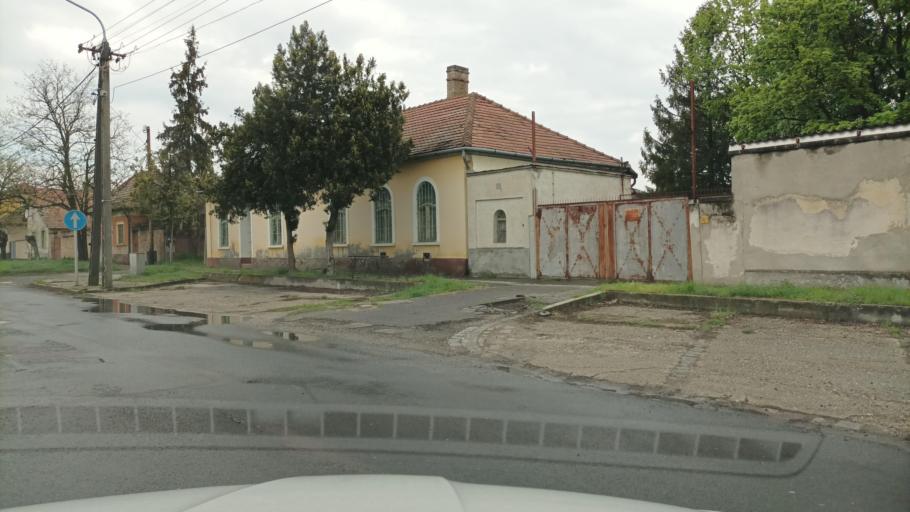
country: HU
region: Pest
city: Nagykoros
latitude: 47.0350
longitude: 19.7630
